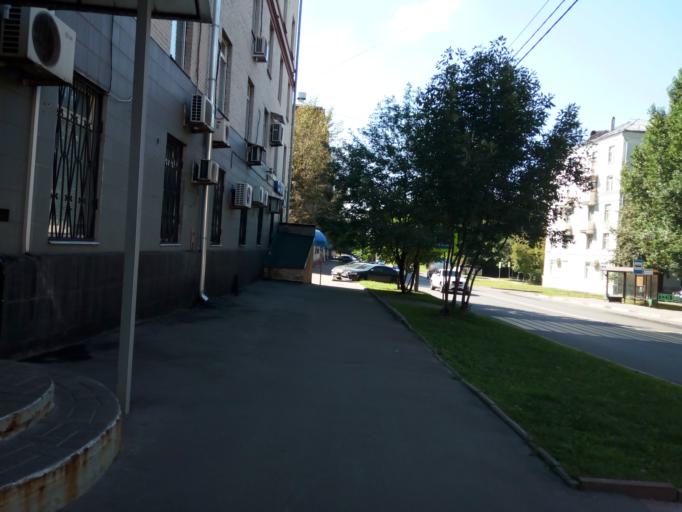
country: RU
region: Moscow
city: Sokol
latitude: 55.7734
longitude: 37.5270
